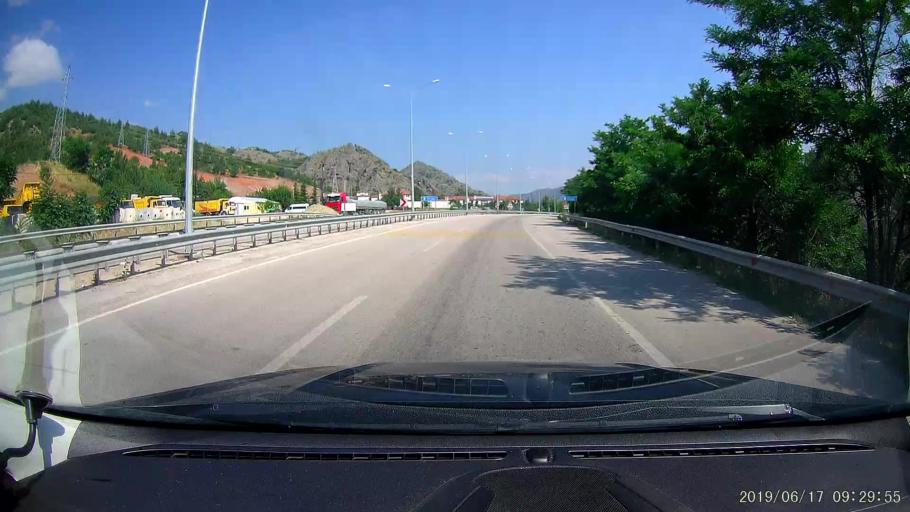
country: TR
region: Amasya
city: Amasya
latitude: 40.7003
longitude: 35.8068
